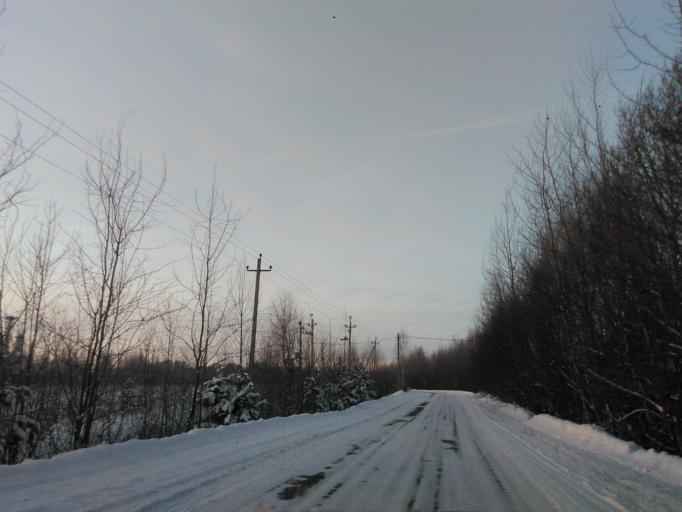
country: RU
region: Tverskaya
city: Konakovo
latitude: 56.6457
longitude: 36.6343
